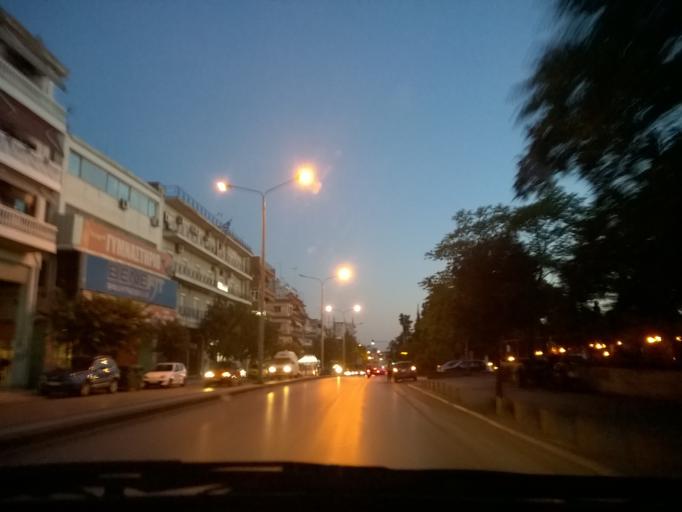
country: GR
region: Central Macedonia
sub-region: Nomos Thessalonikis
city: Thessaloniki
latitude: 40.6513
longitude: 22.9353
